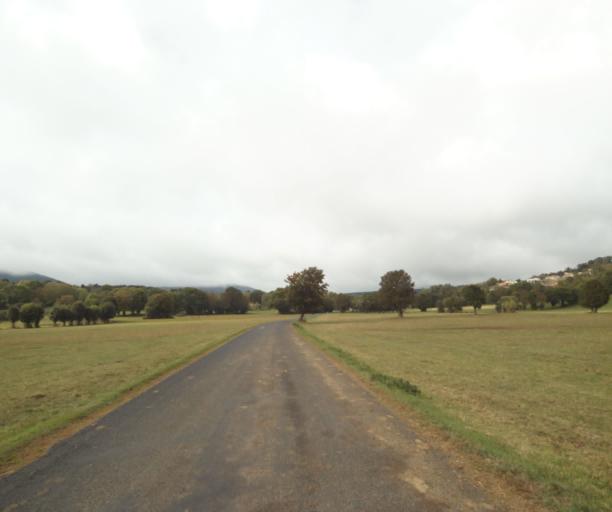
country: FR
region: Auvergne
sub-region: Departement du Puy-de-Dome
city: Saint-Genes-Champanelle
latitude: 45.7129
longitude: 2.9976
